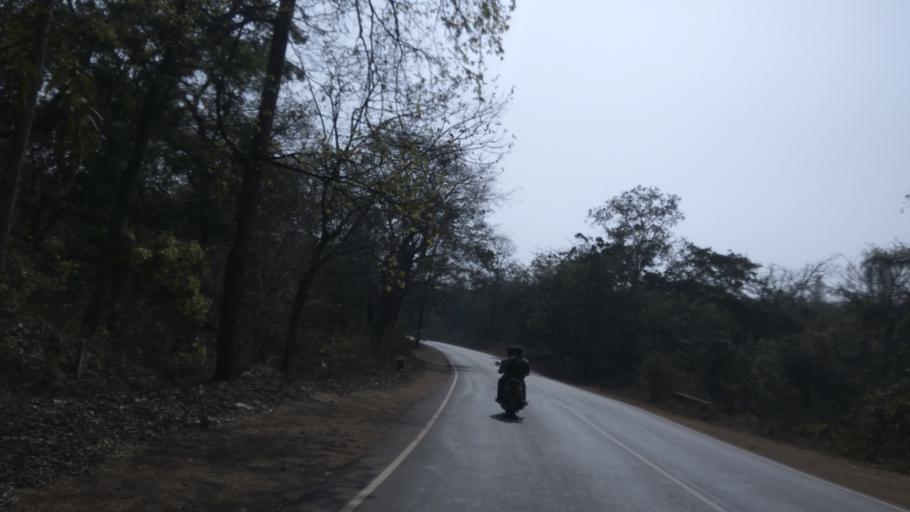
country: IN
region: Goa
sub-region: North Goa
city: Palle
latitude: 15.3789
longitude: 74.1473
